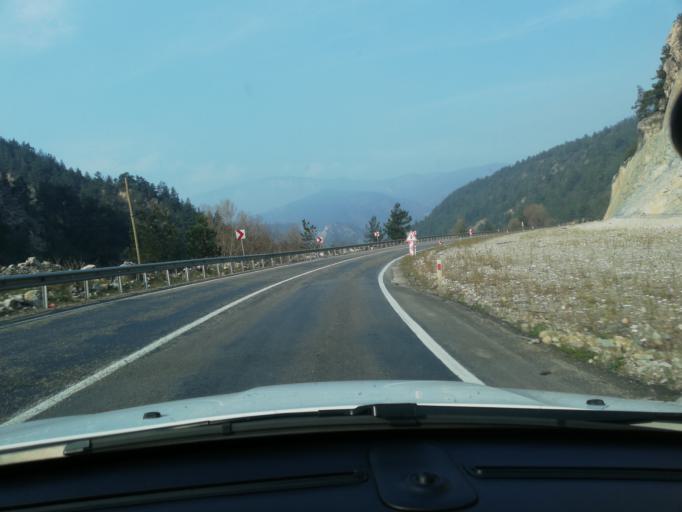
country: TR
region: Karabuk
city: Karabuk
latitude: 41.1586
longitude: 32.5511
